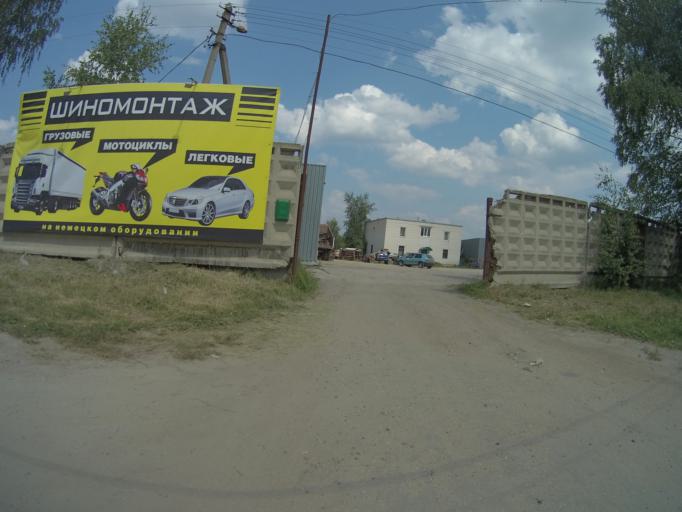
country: RU
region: Vladimir
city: Kommunar
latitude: 56.0479
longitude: 40.5350
